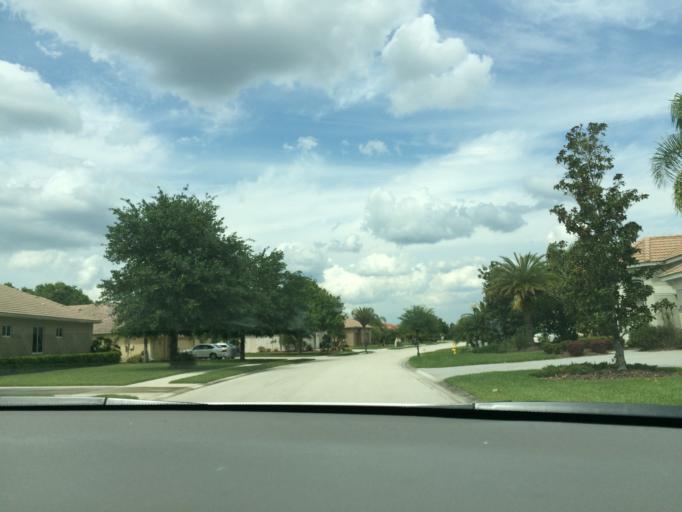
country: US
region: Florida
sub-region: Manatee County
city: Ellenton
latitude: 27.4994
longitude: -82.4127
